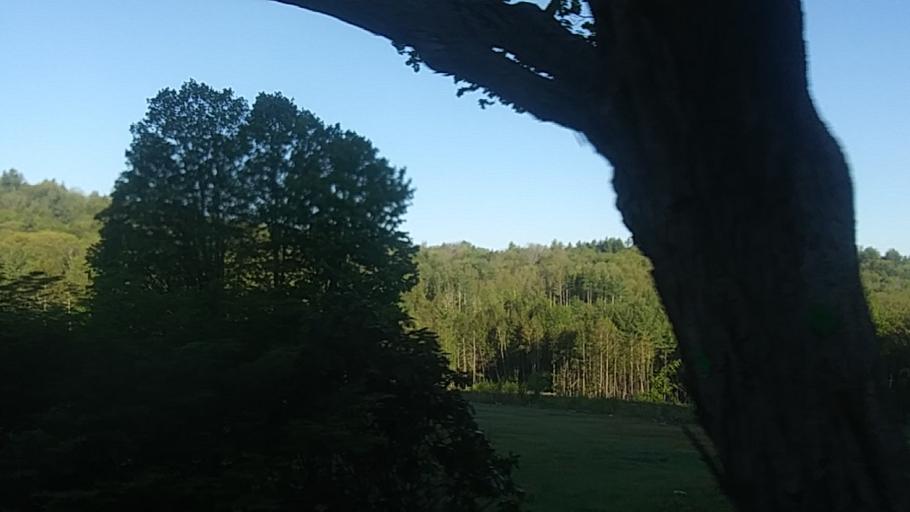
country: US
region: Massachusetts
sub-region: Franklin County
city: Shelburne Falls
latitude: 42.5990
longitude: -72.7597
